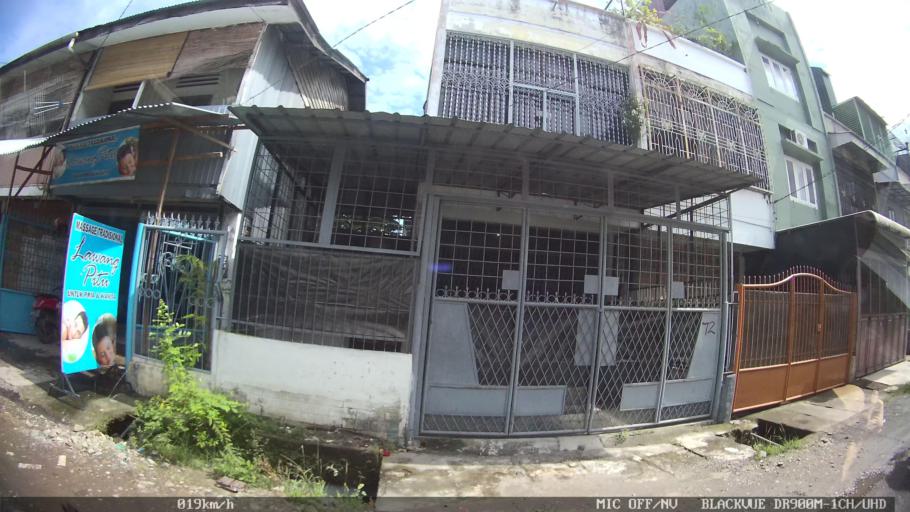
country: ID
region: North Sumatra
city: Medan
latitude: 3.5876
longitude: 98.7079
